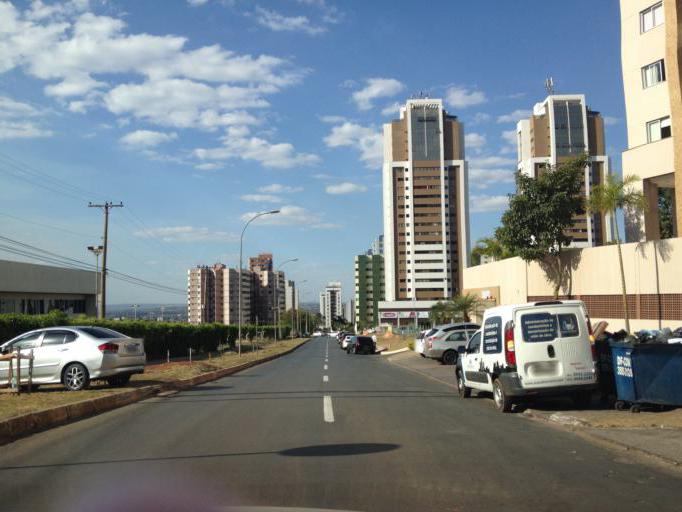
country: BR
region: Federal District
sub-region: Brasilia
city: Brasilia
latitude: -15.8326
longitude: -48.0372
